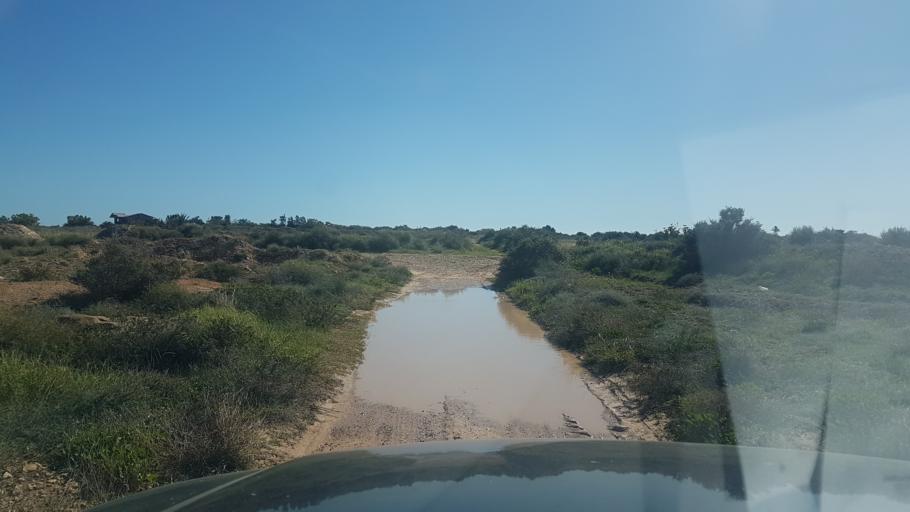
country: TN
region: Safaqis
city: Al Qarmadah
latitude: 34.6702
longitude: 11.0682
